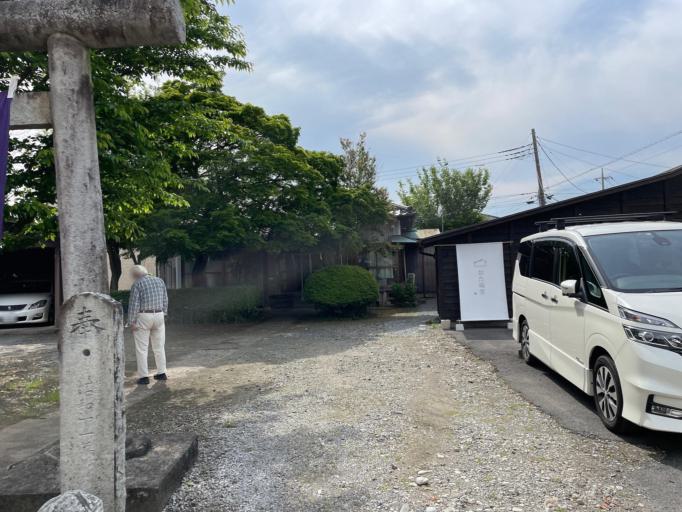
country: JP
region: Tochigi
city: Tochigi
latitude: 36.3887
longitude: 139.7334
